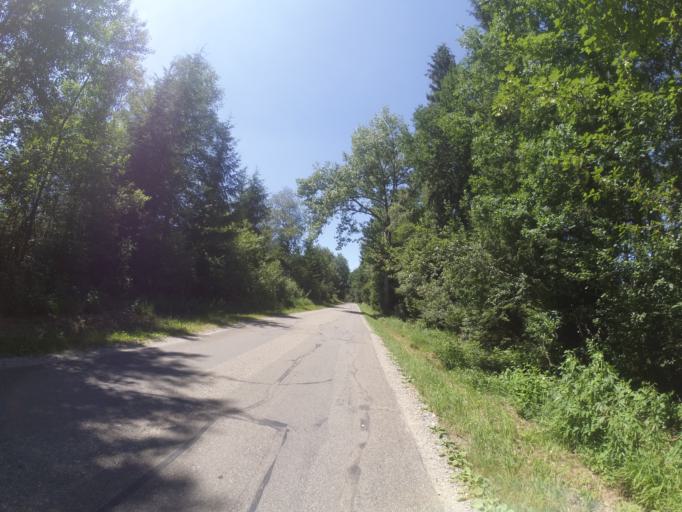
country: DE
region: Baden-Wuerttemberg
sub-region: Tuebingen Region
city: Bad Waldsee
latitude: 47.9196
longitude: 9.7176
